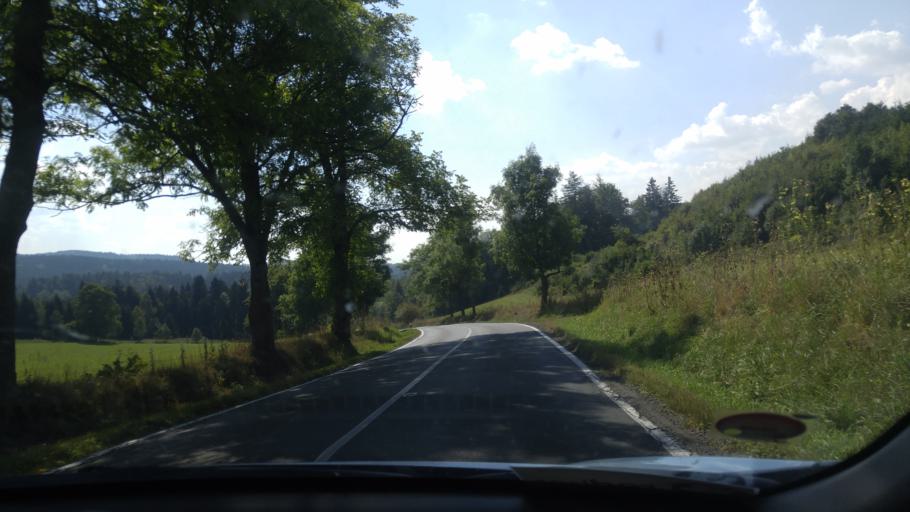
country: CZ
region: Olomoucky
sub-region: Okres Sumperk
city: Stare Mesto
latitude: 50.1787
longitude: 17.0423
